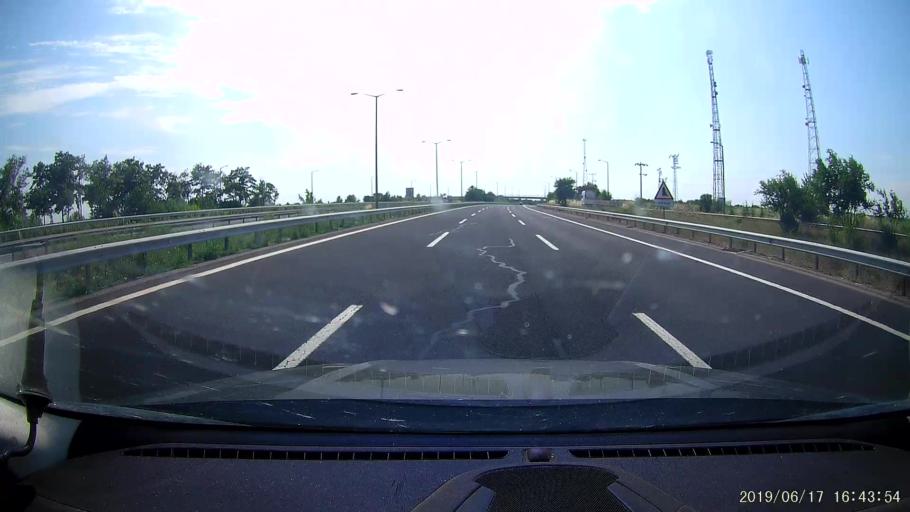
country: TR
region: Kirklareli
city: Luleburgaz
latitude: 41.4792
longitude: 27.2782
